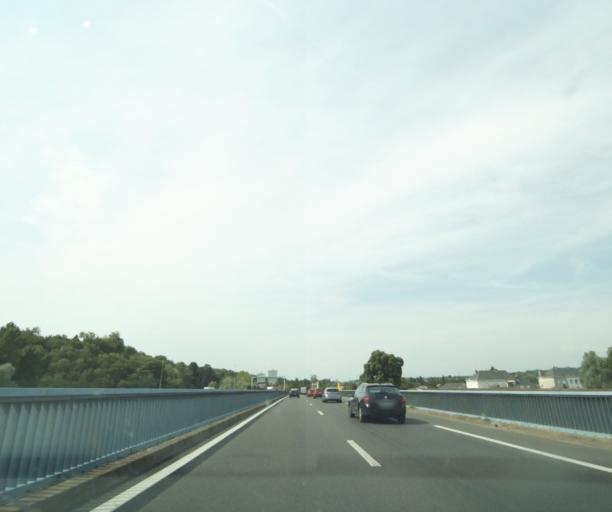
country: FR
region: Centre
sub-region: Departement d'Indre-et-Loire
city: Saint-Cyr-sur-Loire
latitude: 47.3923
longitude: 0.6477
